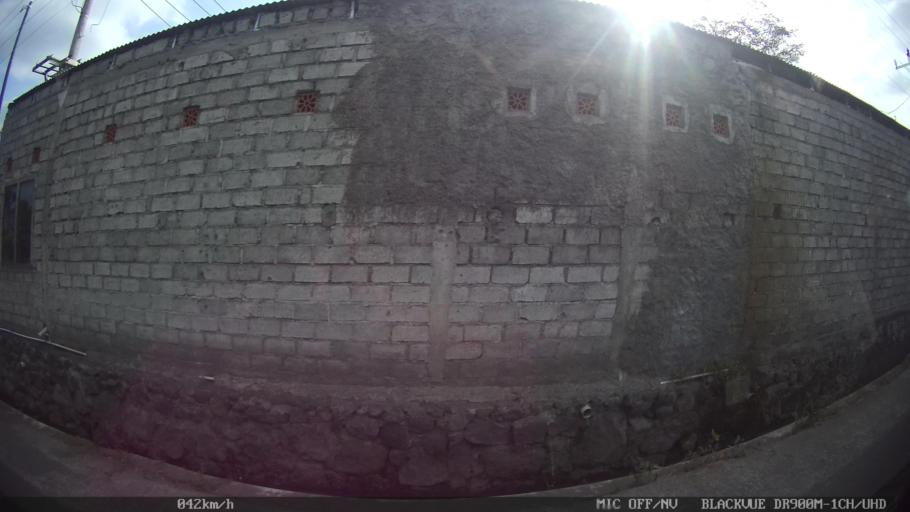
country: ID
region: Central Java
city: Candi Prambanan
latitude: -7.6854
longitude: 110.4605
